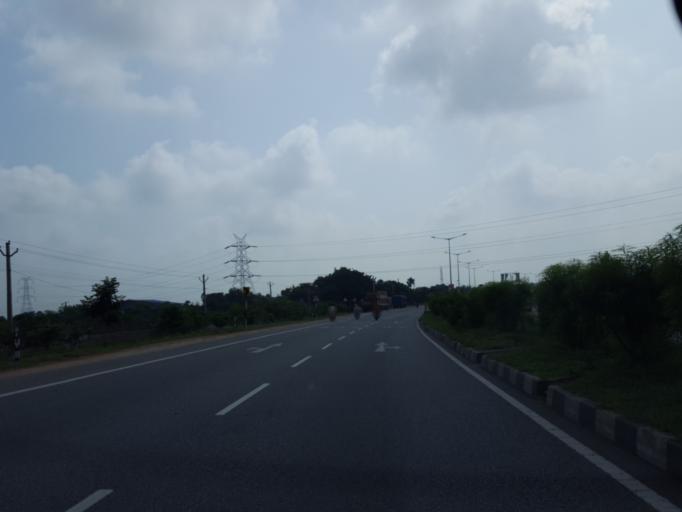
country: IN
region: Telangana
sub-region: Nalgonda
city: Gudur
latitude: 17.2641
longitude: 78.8365
